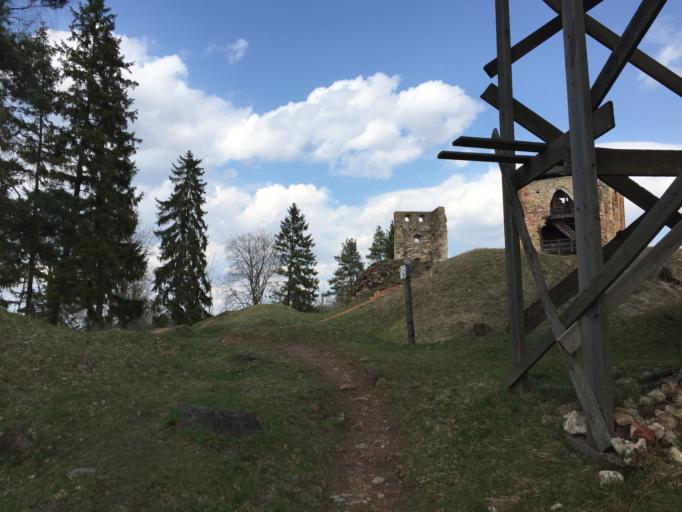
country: RU
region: Pskov
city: Pechory
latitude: 57.7302
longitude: 27.3611
